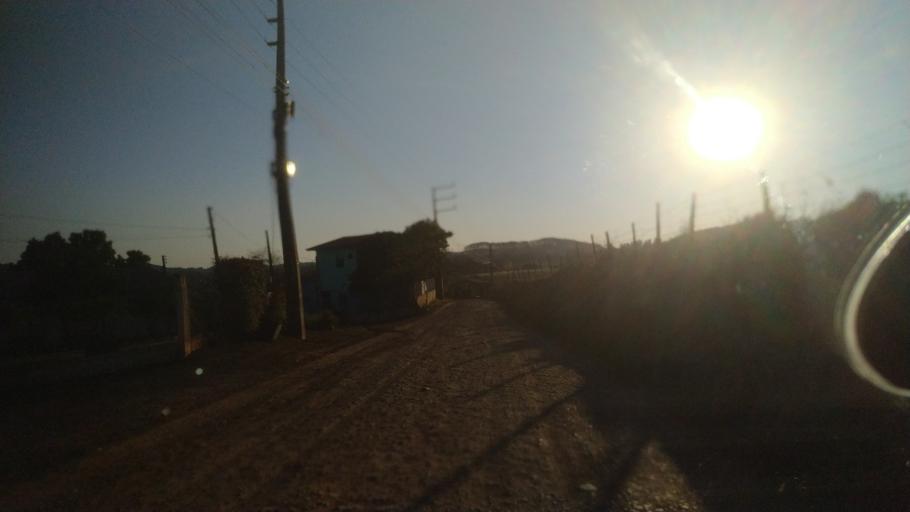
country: BR
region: Santa Catarina
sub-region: Chapeco
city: Chapeco
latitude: -27.0381
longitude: -52.6315
